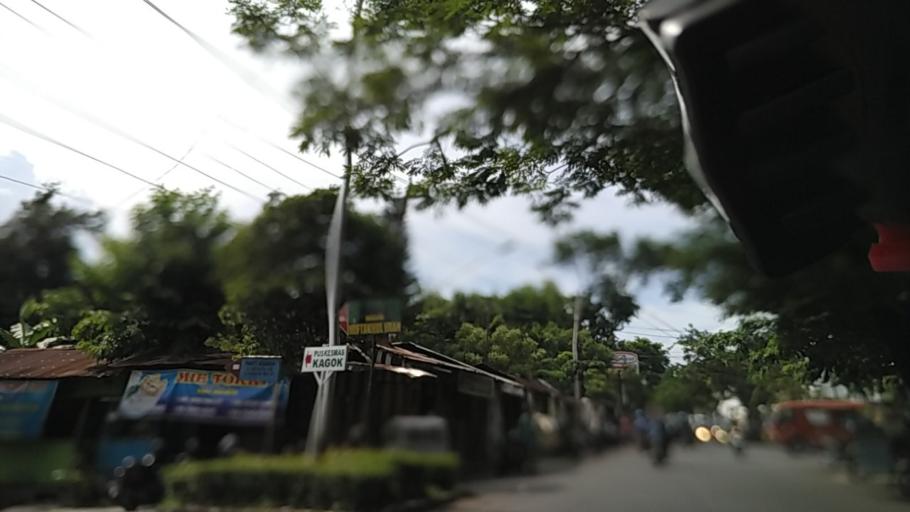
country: ID
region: Central Java
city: Semarang
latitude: -7.0085
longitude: 110.4187
